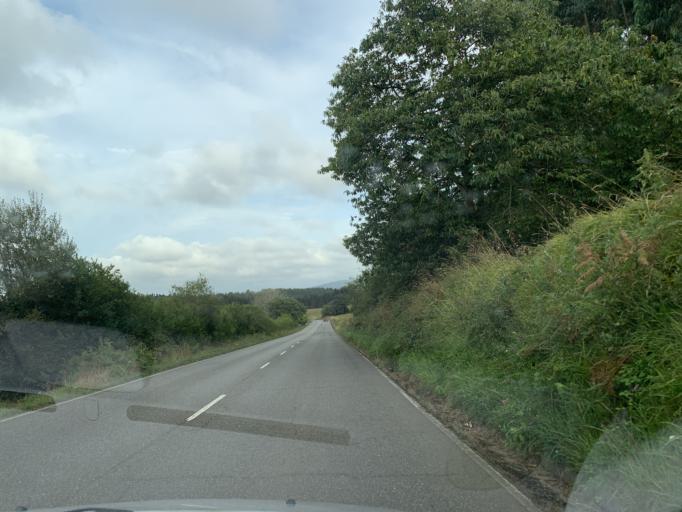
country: ES
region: Asturias
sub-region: Province of Asturias
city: Villaviciosa
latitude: 43.5174
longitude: -5.4337
